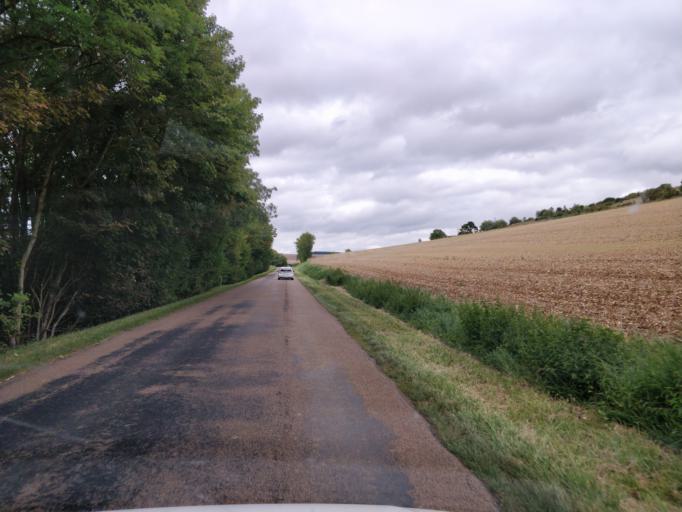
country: FR
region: Champagne-Ardenne
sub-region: Departement de l'Aube
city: Aix-en-Othe
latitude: 48.1933
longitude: 3.6325
